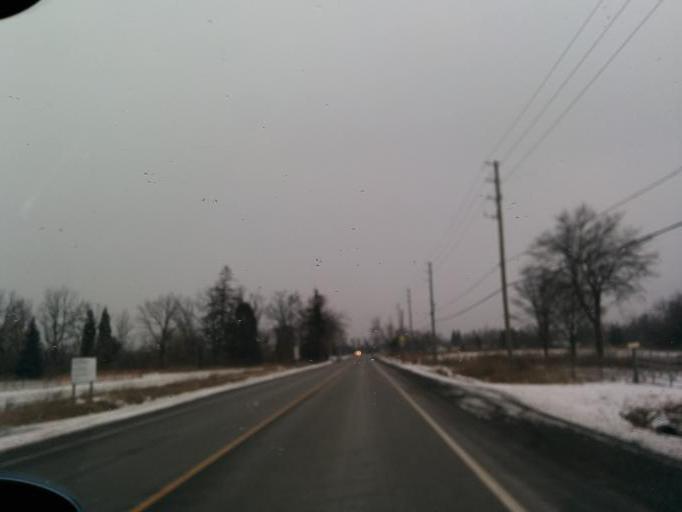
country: CA
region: Ontario
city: Brampton
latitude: 43.6388
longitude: -79.8116
